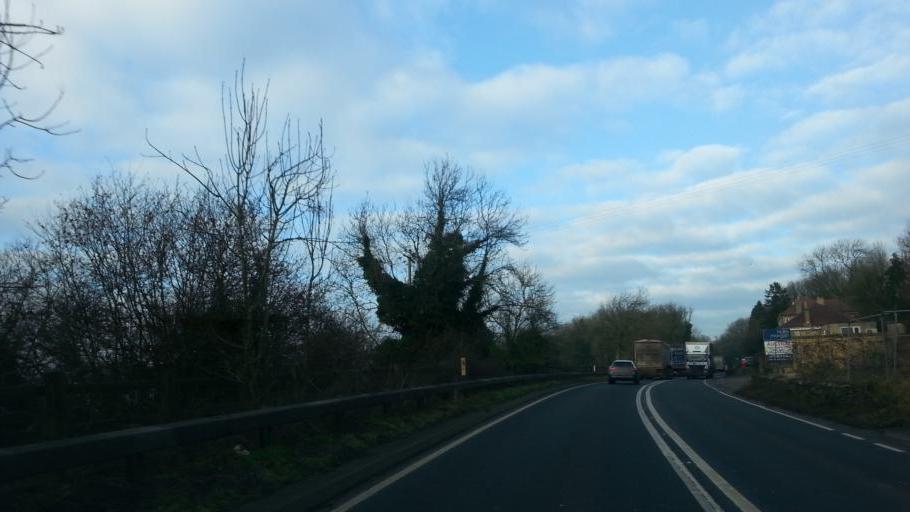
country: GB
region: England
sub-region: South Gloucestershire
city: Cold Ashton
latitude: 51.4258
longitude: -2.3570
